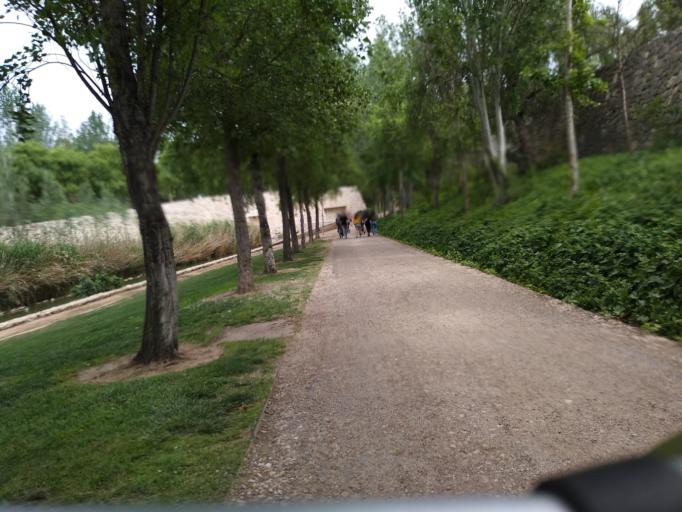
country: ES
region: Valencia
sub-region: Provincia de Valencia
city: Mislata
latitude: 39.4741
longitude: -0.4083
